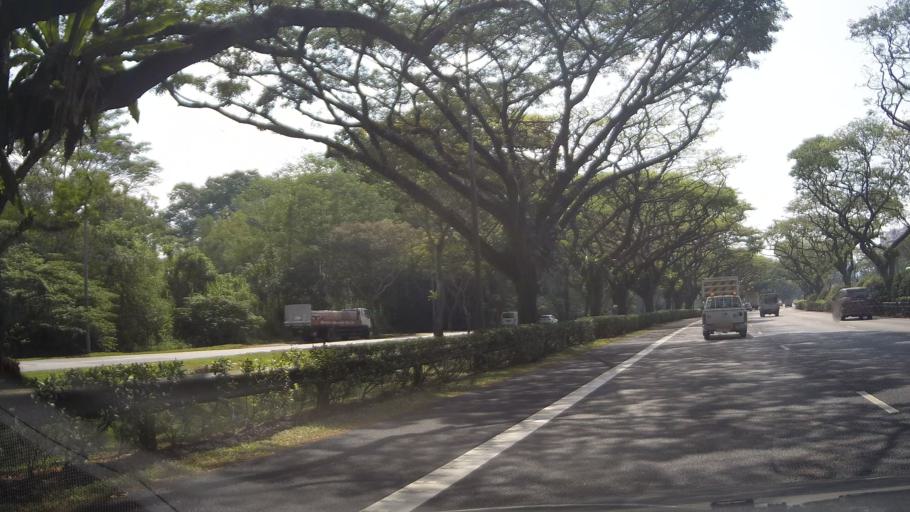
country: MY
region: Johor
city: Johor Bahru
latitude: 1.3547
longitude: 103.7262
